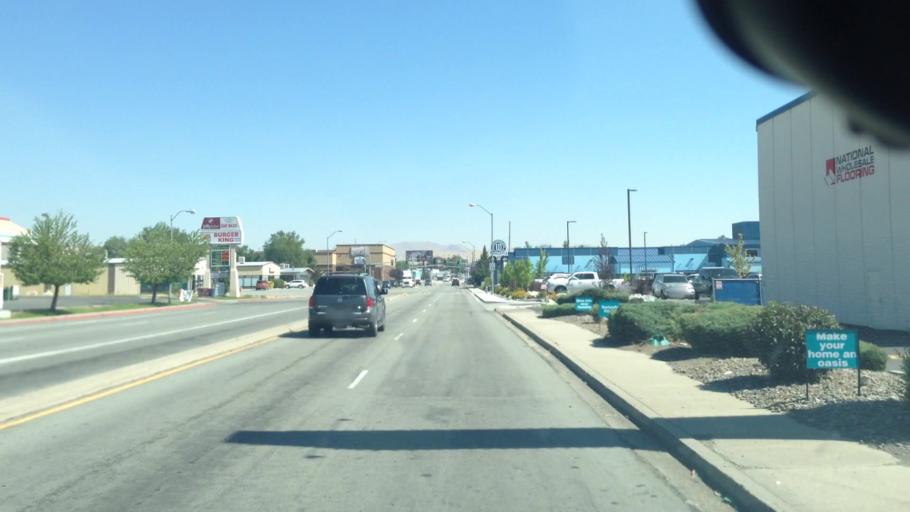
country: US
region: Nevada
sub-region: Washoe County
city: Sparks
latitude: 39.5236
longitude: -119.7667
